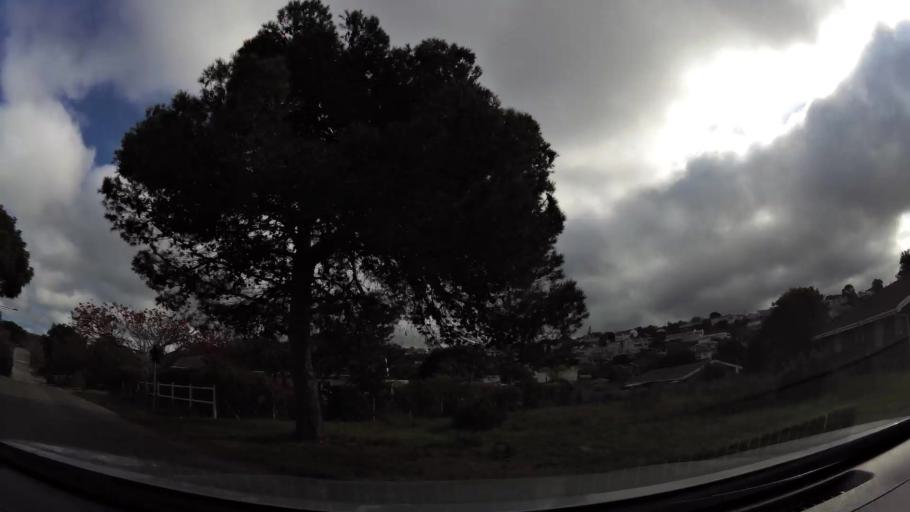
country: ZA
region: Western Cape
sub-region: Eden District Municipality
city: Plettenberg Bay
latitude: -34.0689
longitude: 23.3705
